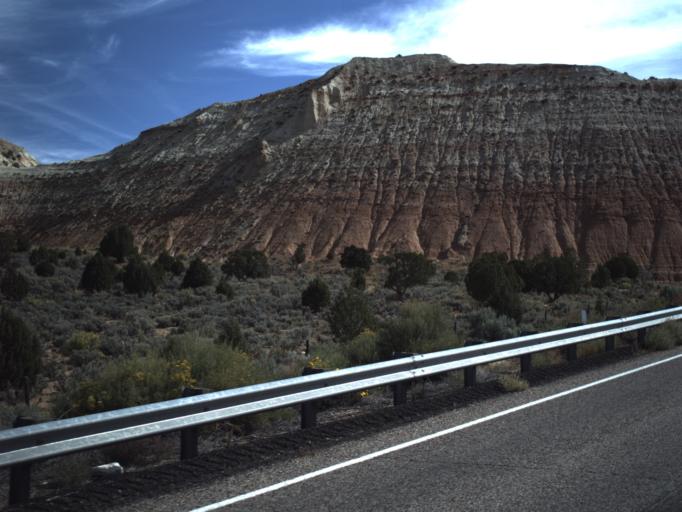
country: US
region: Utah
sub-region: Garfield County
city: Panguitch
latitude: 37.5645
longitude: -112.0417
